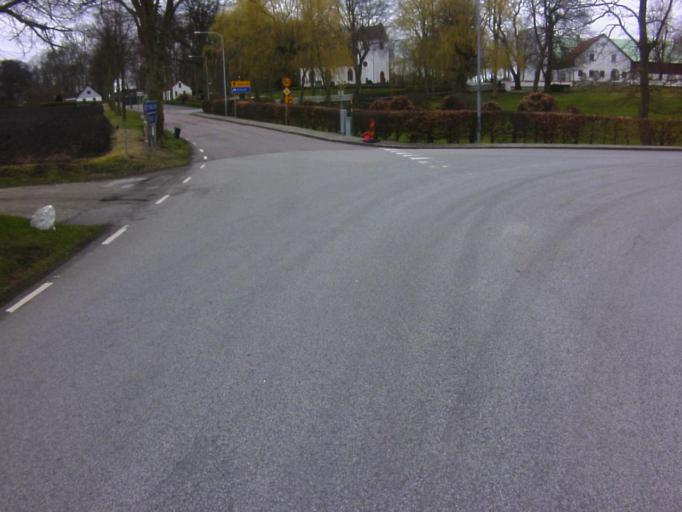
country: SE
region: Skane
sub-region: Kavlinge Kommun
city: Kaevlinge
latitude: 55.7627
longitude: 13.0698
